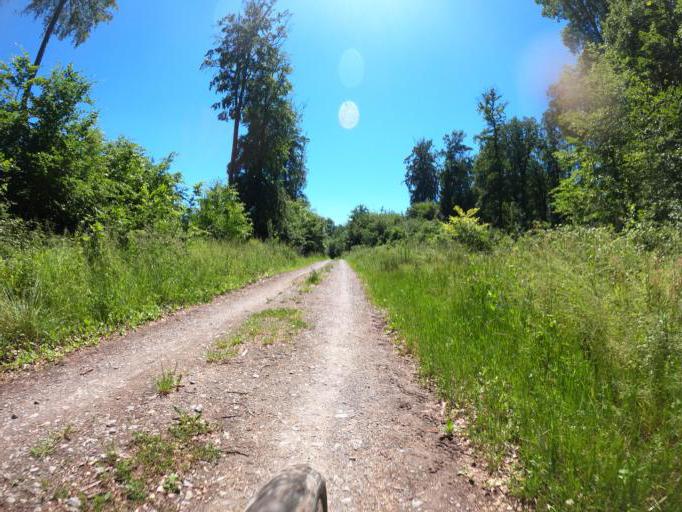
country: DE
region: Baden-Wuerttemberg
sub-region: Regierungsbezirk Stuttgart
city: Sersheim
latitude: 49.0029
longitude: 8.9904
